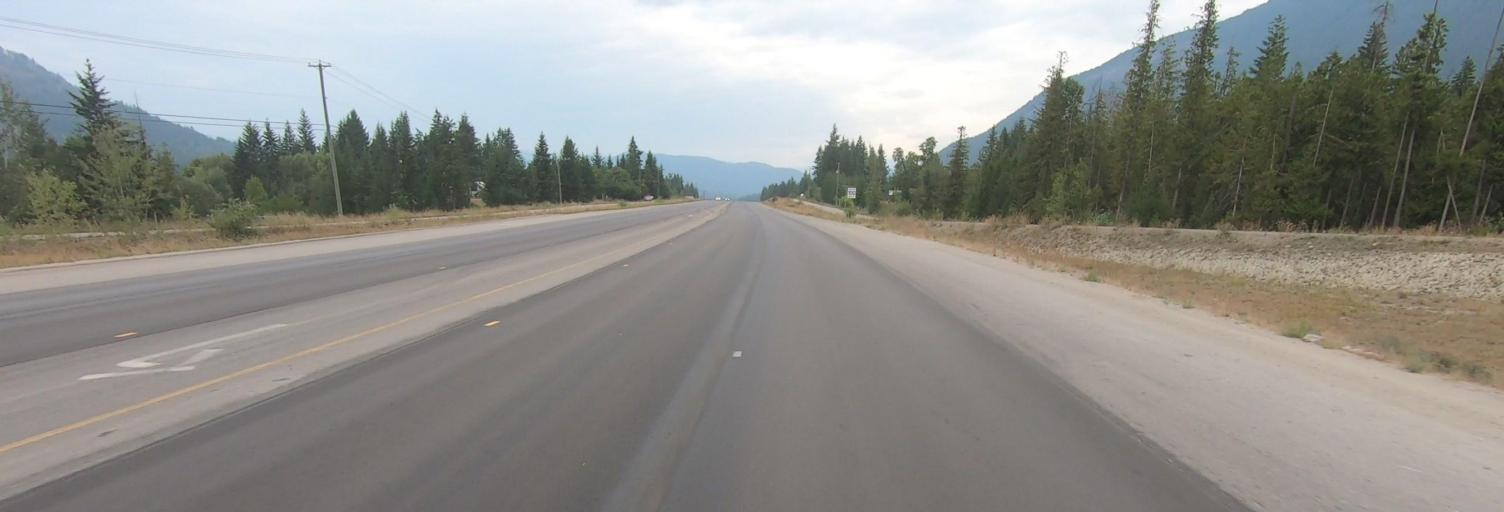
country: CA
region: British Columbia
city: Salmon Arm
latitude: 50.8096
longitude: -119.3199
